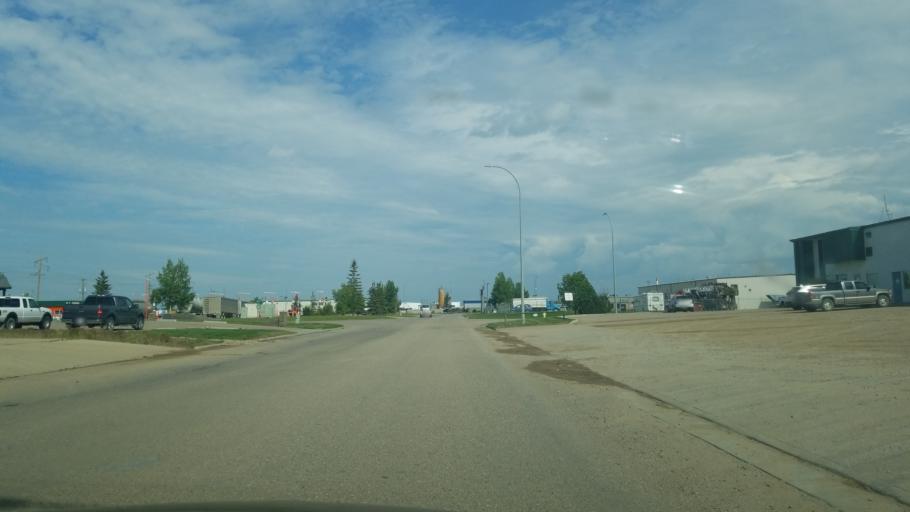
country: CA
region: Saskatchewan
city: Lloydminster
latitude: 53.2914
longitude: -110.0381
